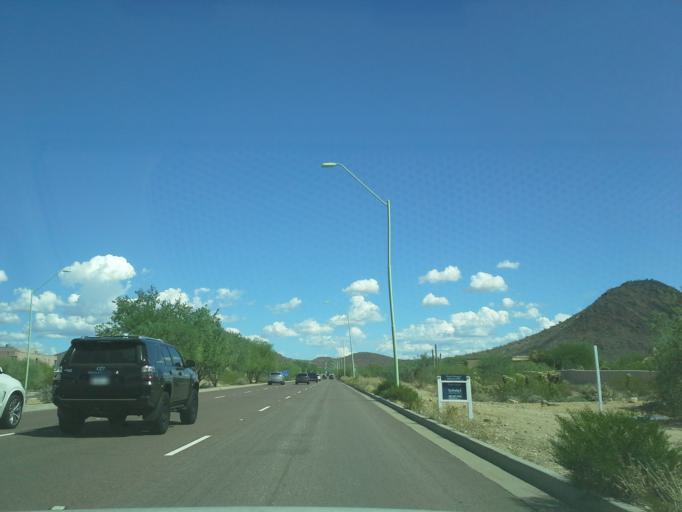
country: US
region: Arizona
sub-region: Maricopa County
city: Fountain Hills
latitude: 33.5823
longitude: -111.7977
